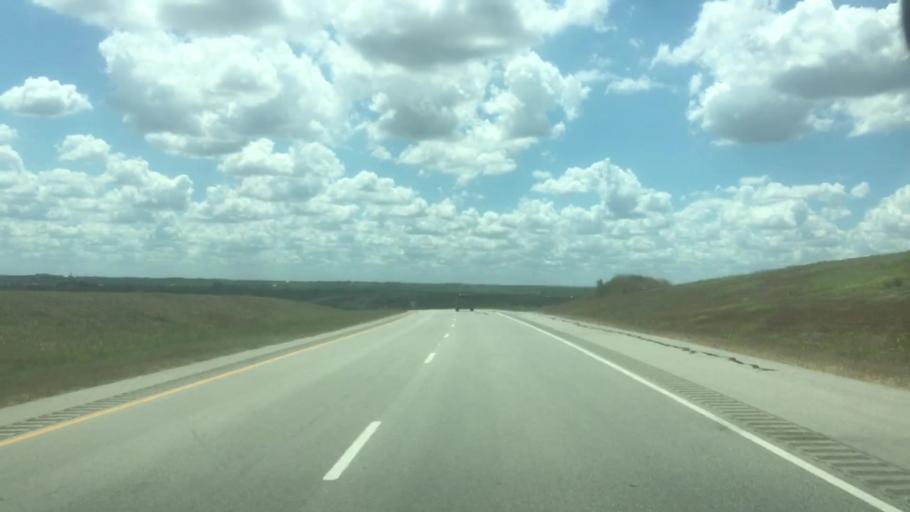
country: US
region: Texas
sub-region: Caldwell County
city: Lockhart
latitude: 29.8483
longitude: -97.7257
